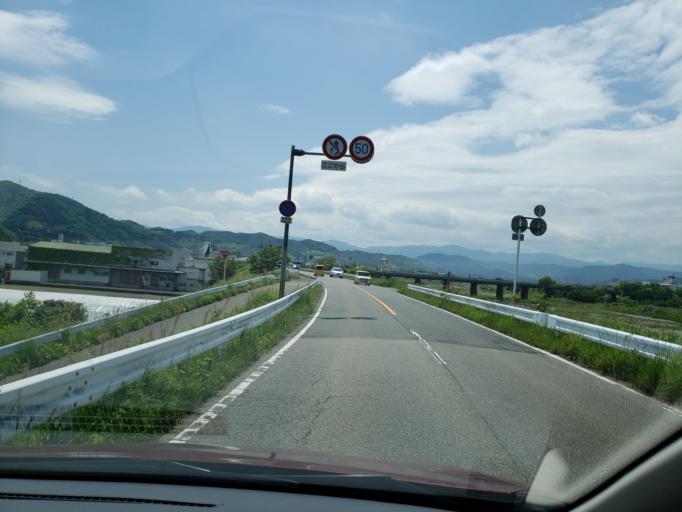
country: JP
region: Tokushima
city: Tokushima-shi
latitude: 34.0788
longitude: 134.5023
